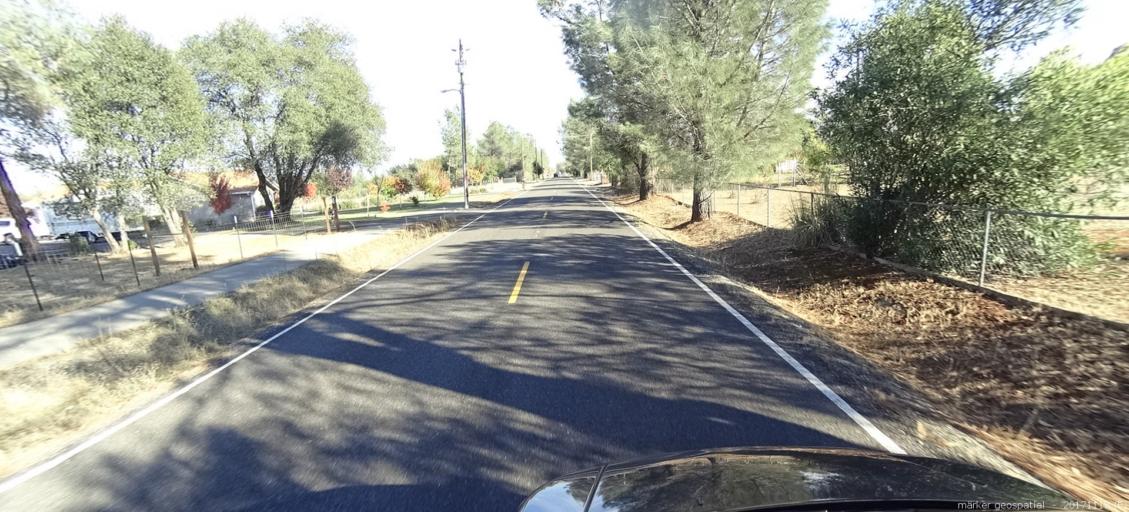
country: US
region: California
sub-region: Shasta County
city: Anderson
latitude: 40.4464
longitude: -122.4244
